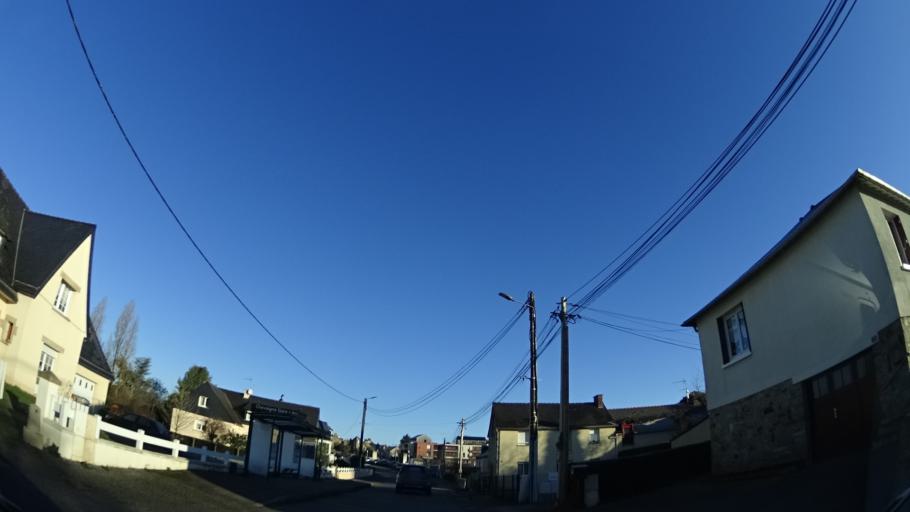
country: FR
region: Brittany
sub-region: Departement d'Ille-et-Vilaine
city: Chevaigne
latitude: 48.2075
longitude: -1.6309
